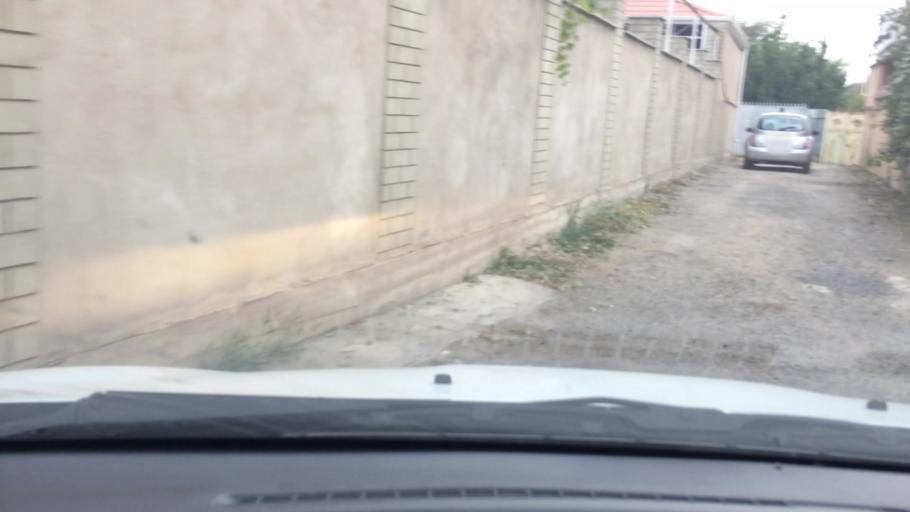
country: GE
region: Kvemo Kartli
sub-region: Marneuli
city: Marneuli
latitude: 41.4818
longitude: 44.7988
